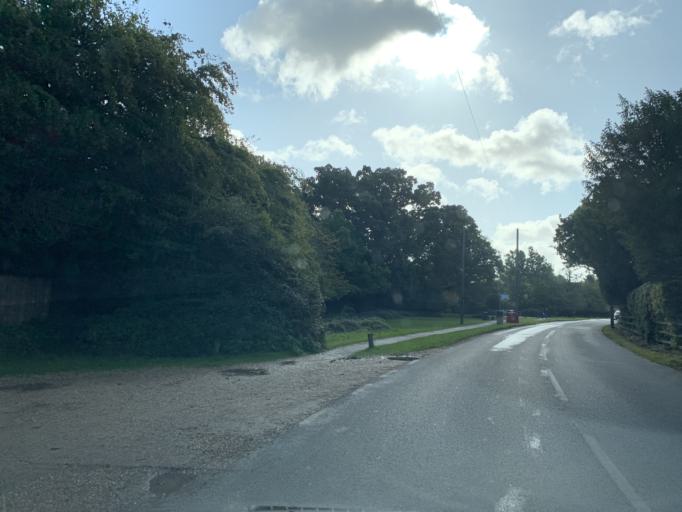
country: GB
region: England
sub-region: Hampshire
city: Brockenhurst
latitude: 50.8213
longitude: -1.5801
